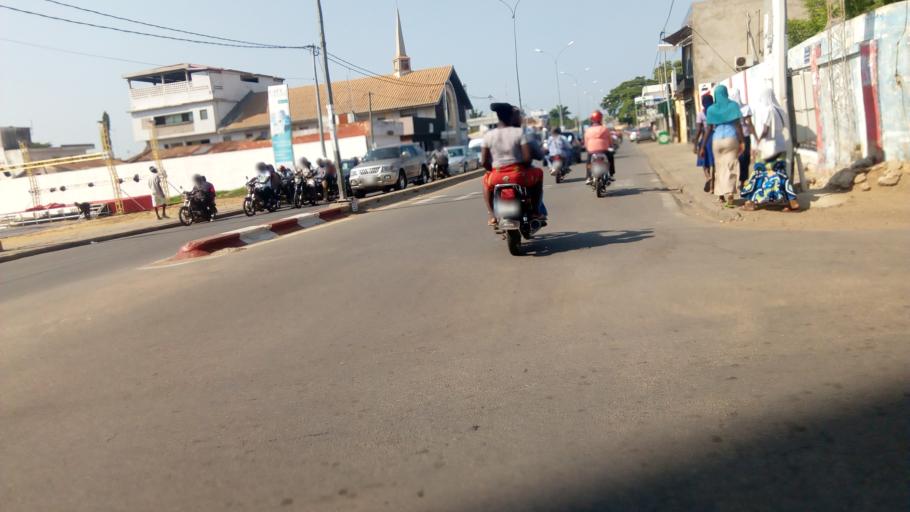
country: TG
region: Maritime
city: Lome
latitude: 6.1337
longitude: 1.2156
